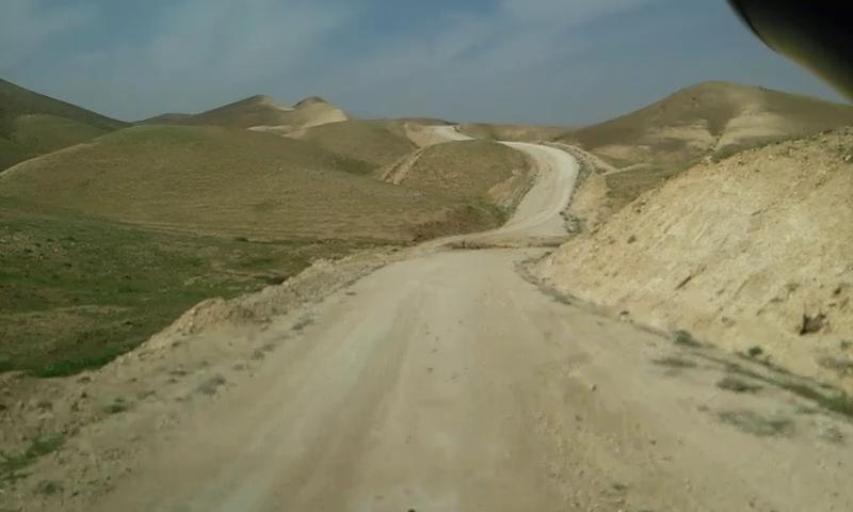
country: PS
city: `Arab ar Rashaydah
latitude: 31.4836
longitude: 35.2781
